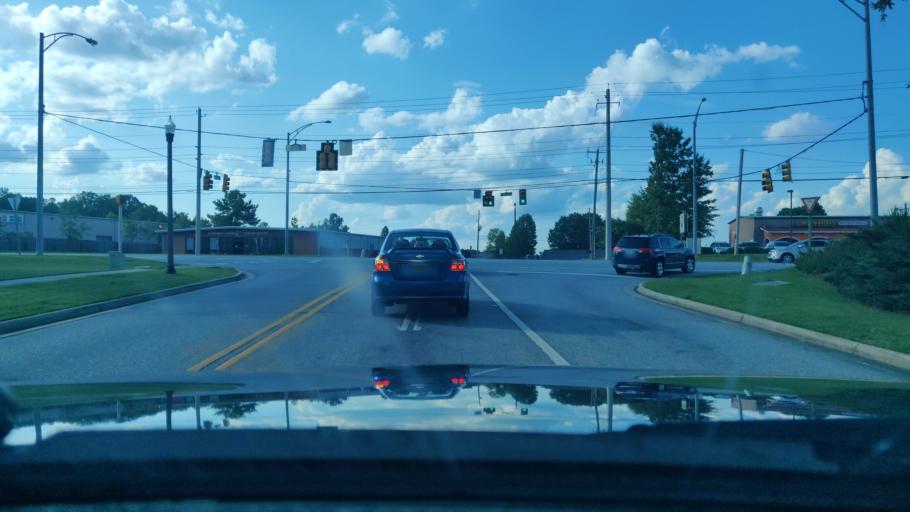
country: US
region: Alabama
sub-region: Lee County
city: Opelika
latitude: 32.6218
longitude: -85.4095
